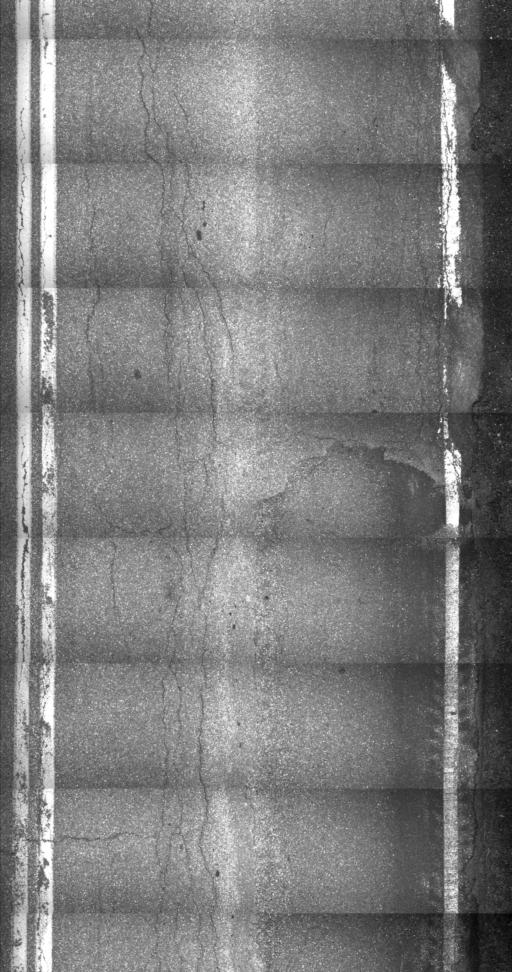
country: US
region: Vermont
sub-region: Orleans County
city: Newport
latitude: 44.7946
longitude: -72.0894
